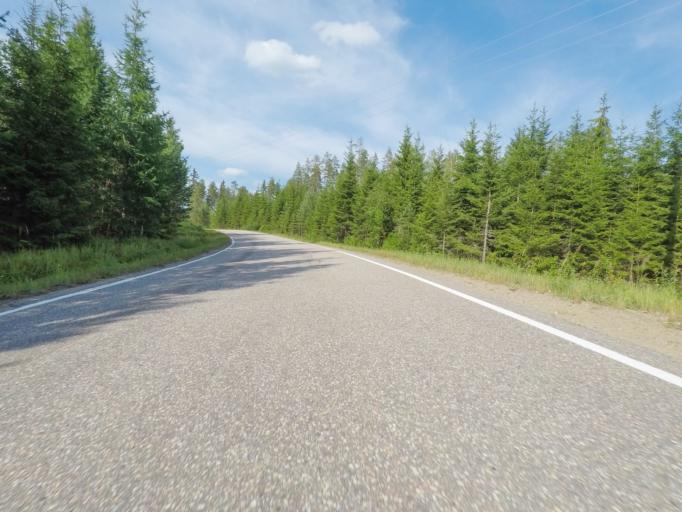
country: FI
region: Southern Savonia
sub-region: Savonlinna
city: Sulkava
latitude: 61.7707
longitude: 28.2377
